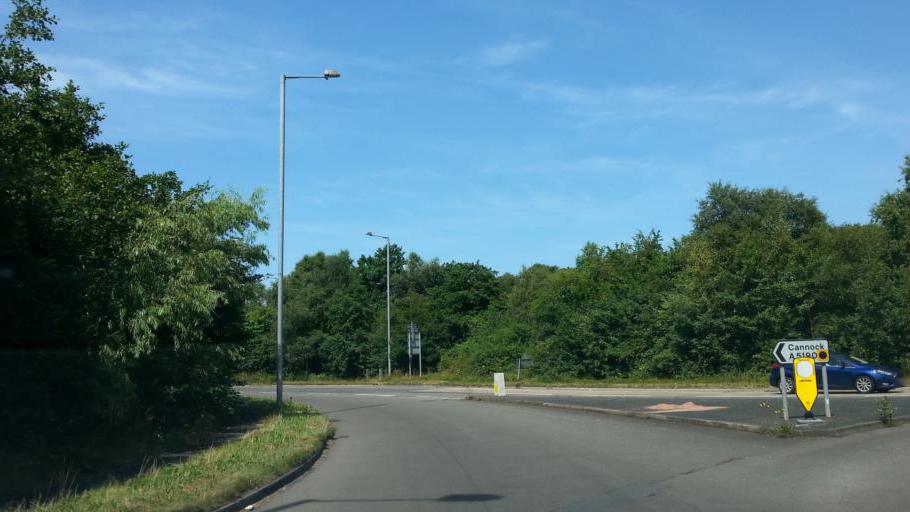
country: GB
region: England
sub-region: Staffordshire
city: Norton Canes
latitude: 52.6840
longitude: -1.9541
